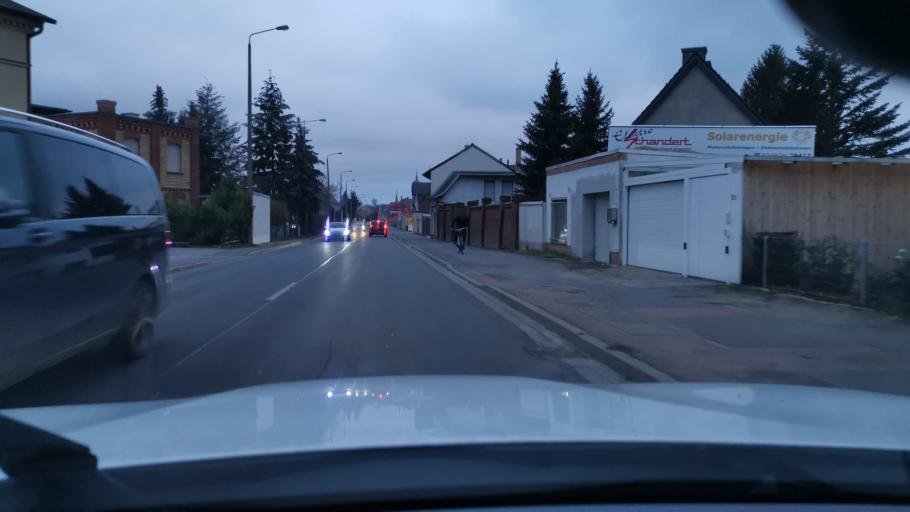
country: DE
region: Saxony-Anhalt
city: Wittenburg
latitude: 51.8760
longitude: 12.6327
